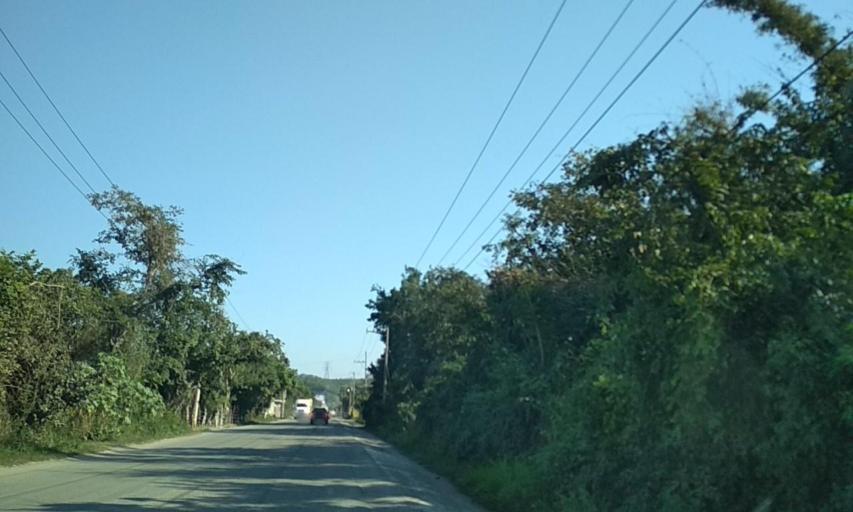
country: MX
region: Veracruz
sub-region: Papantla
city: El Chote
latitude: 20.4075
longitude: -97.3454
